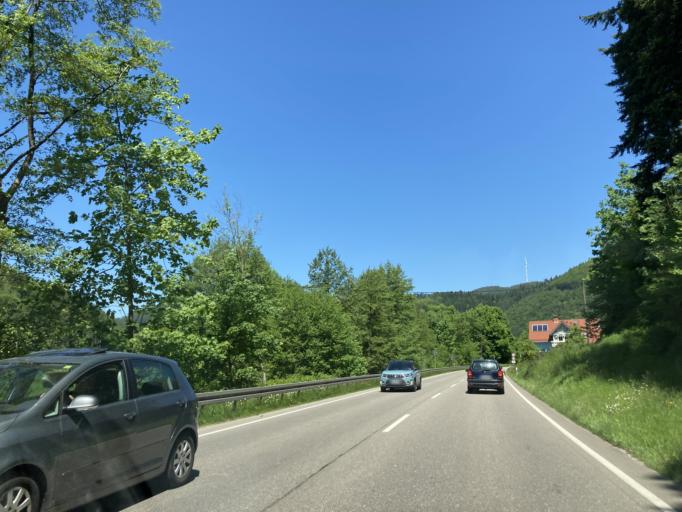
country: DE
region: Baden-Wuerttemberg
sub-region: Freiburg Region
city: Hausach
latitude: 48.2765
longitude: 8.1974
